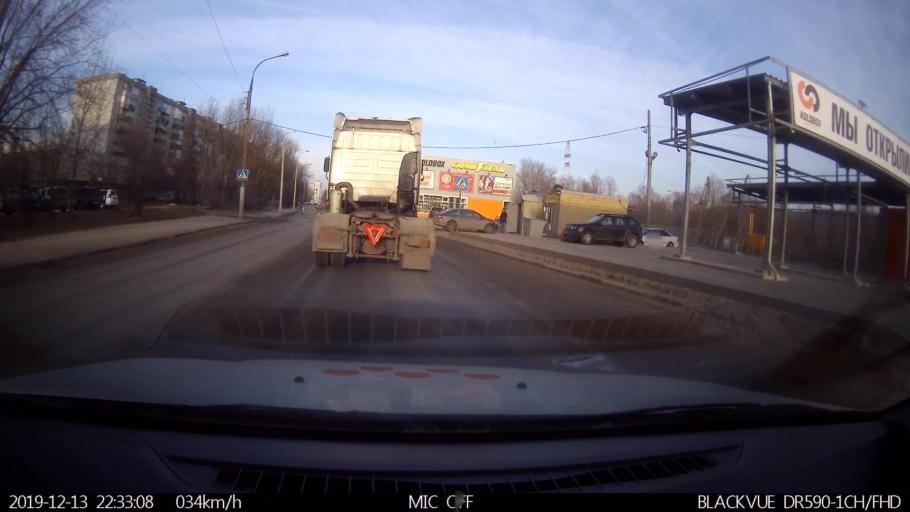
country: RU
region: Nizjnij Novgorod
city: Nizhniy Novgorod
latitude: 56.2863
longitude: 43.9534
